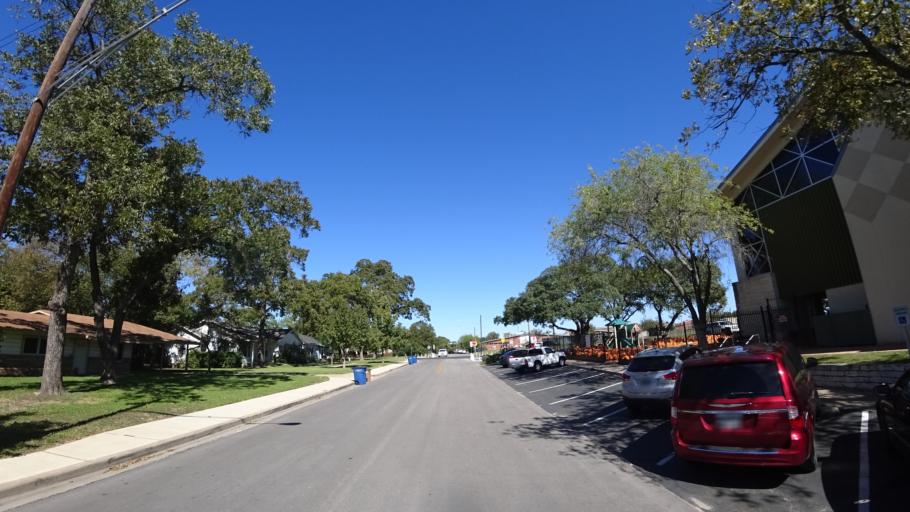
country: US
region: Texas
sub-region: Travis County
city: Austin
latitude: 30.3356
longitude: -97.7418
